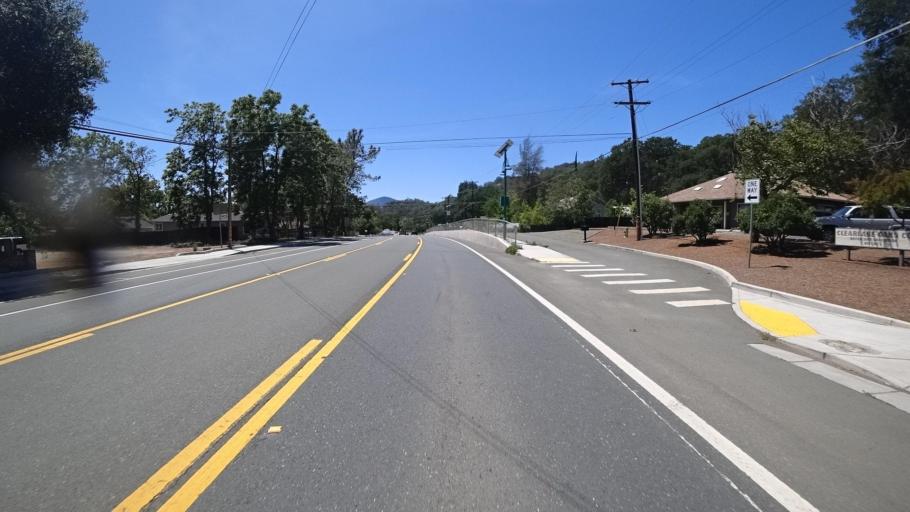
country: US
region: California
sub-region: Lake County
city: Clearlake Oaks
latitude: 39.0276
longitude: -122.6677
